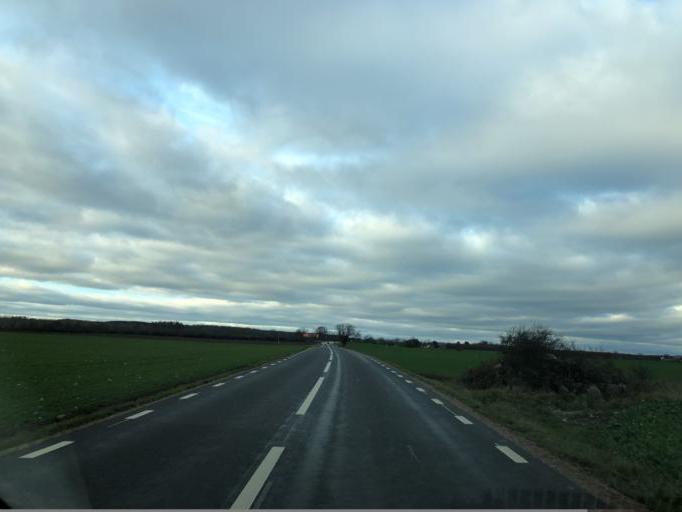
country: SE
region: Skane
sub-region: Svalovs Kommun
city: Svaloev
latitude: 55.9171
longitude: 13.2024
